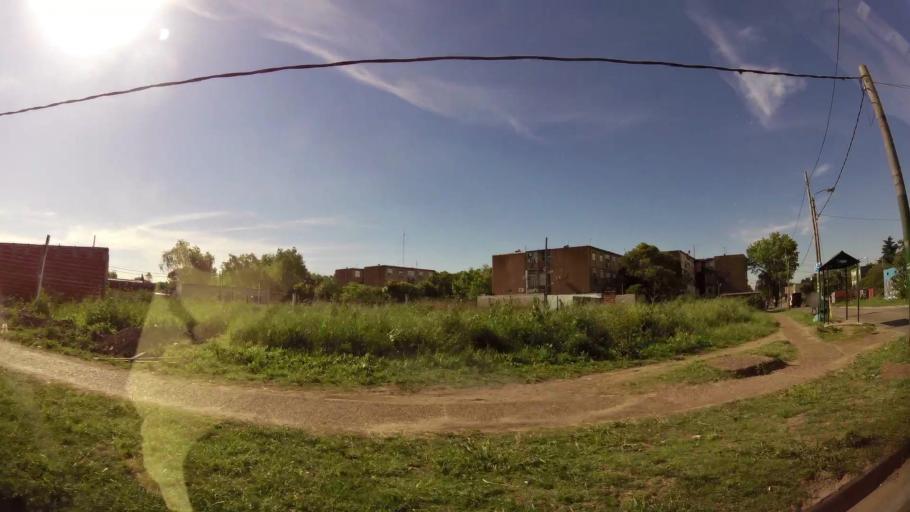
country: AR
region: Buenos Aires
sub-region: Partido de Almirante Brown
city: Adrogue
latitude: -34.8224
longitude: -58.3439
